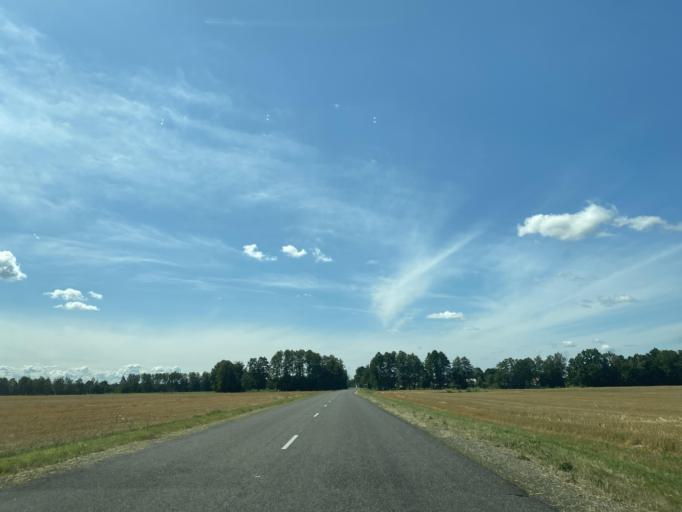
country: BY
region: Brest
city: Ivanava
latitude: 52.1932
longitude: 25.6116
